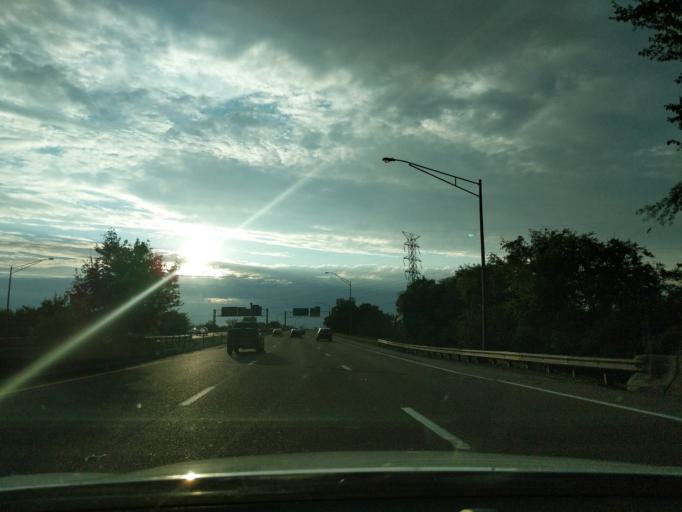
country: US
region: Tennessee
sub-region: Shelby County
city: New South Memphis
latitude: 35.0756
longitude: -90.0397
